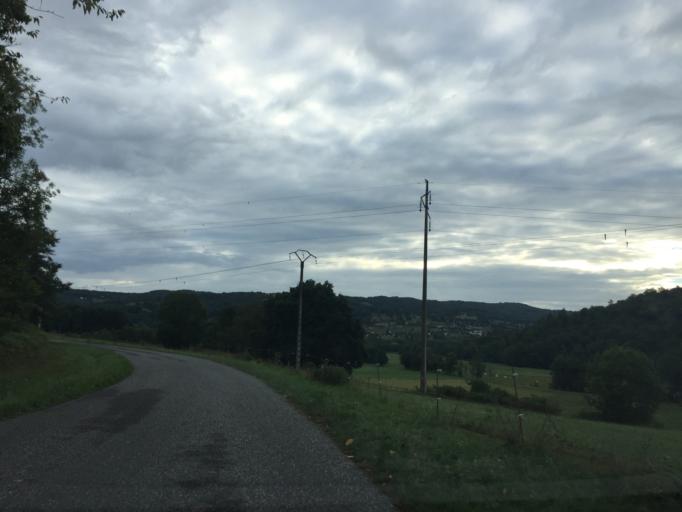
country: FR
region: Midi-Pyrenees
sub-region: Departement des Hautes-Pyrenees
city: Tournay
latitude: 43.1731
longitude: 0.2302
